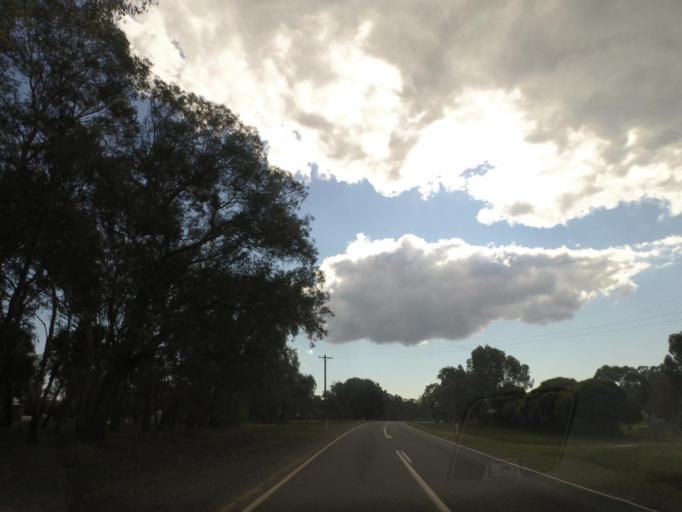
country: AU
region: New South Wales
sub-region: Corowa Shire
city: Howlong
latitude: -36.1839
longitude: 146.6078
